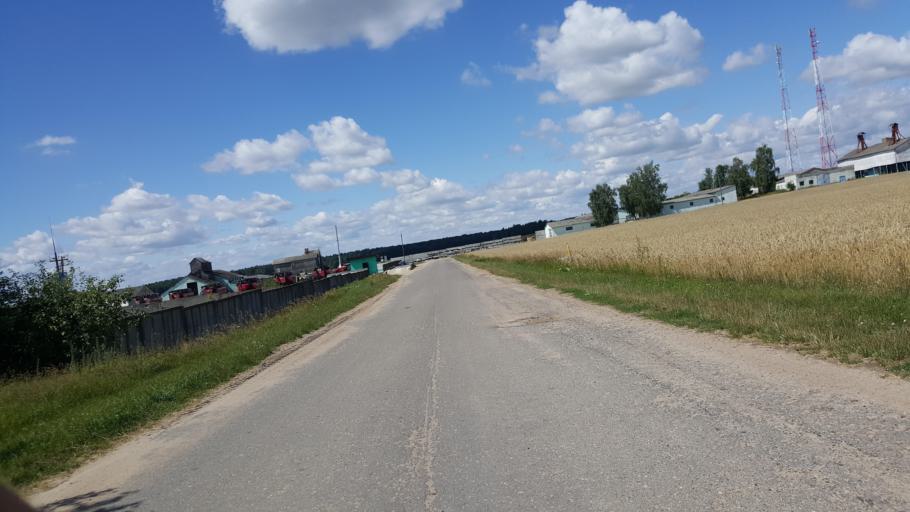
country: BY
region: Brest
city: Kamyanyets
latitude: 52.3366
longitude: 23.9080
